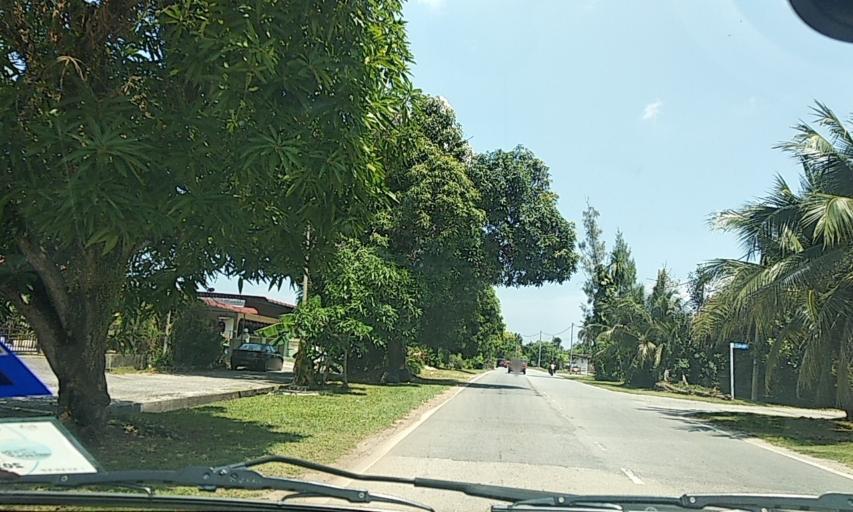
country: MY
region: Kedah
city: Sungai Petani
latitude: 5.6343
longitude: 100.4656
